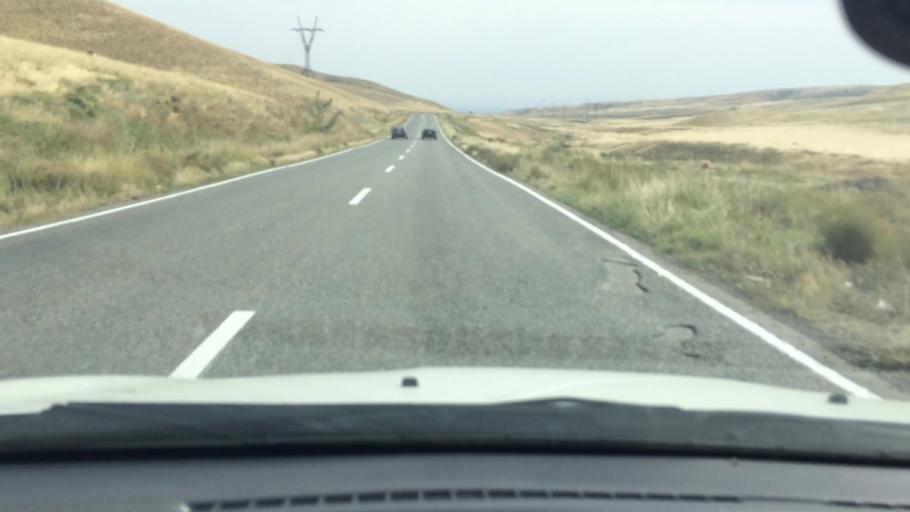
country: GE
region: Kvemo Kartli
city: Rust'avi
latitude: 41.5099
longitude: 44.9489
